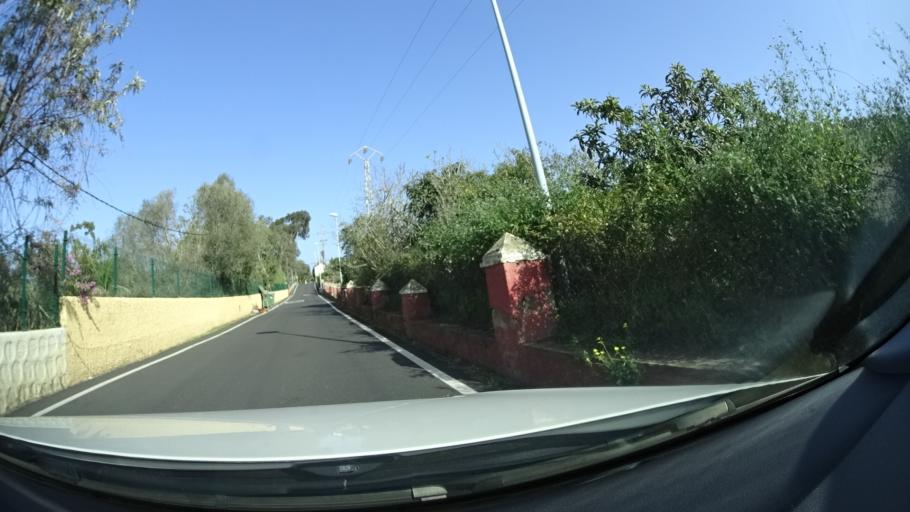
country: ES
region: Canary Islands
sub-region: Provincia de Las Palmas
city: Santa Brigida
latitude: 28.0414
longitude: -15.4728
